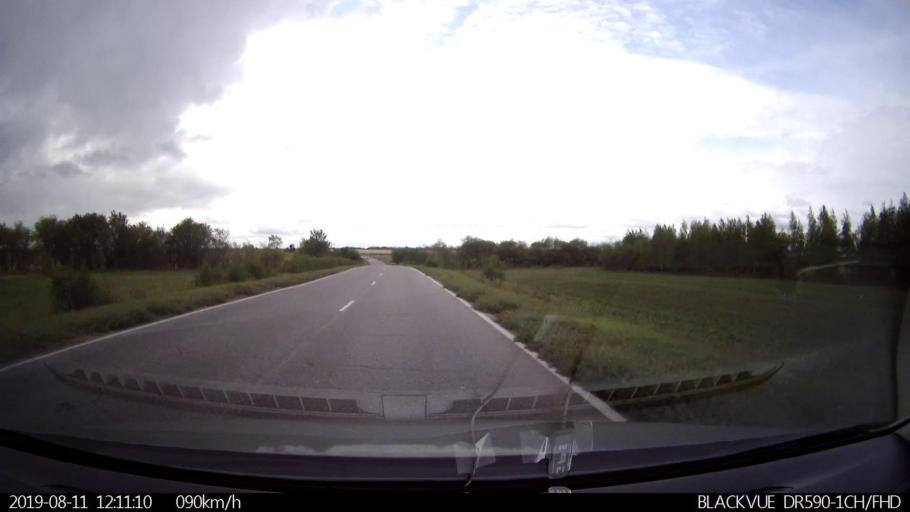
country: RU
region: Ulyanovsk
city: Silikatnyy
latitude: 53.9875
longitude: 48.0087
